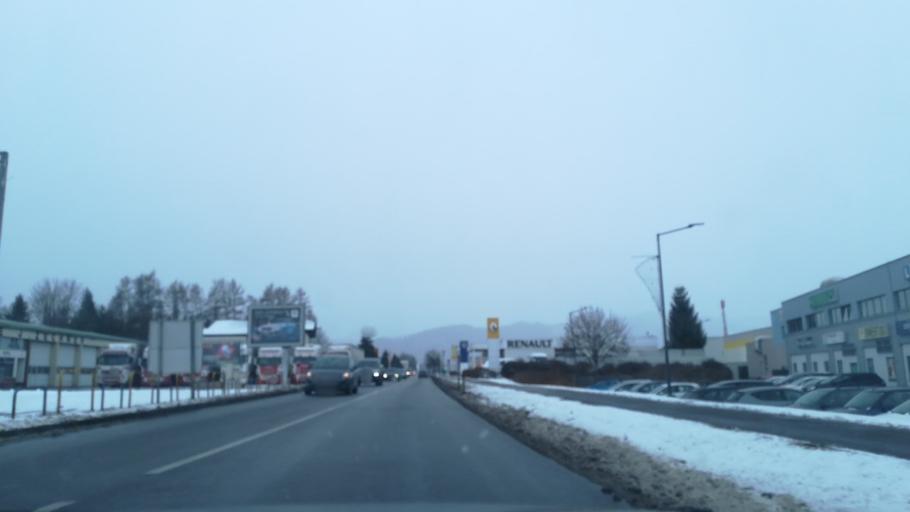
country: AT
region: Styria
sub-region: Politischer Bezirk Murtal
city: Fohnsdorf
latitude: 47.1834
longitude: 14.6813
